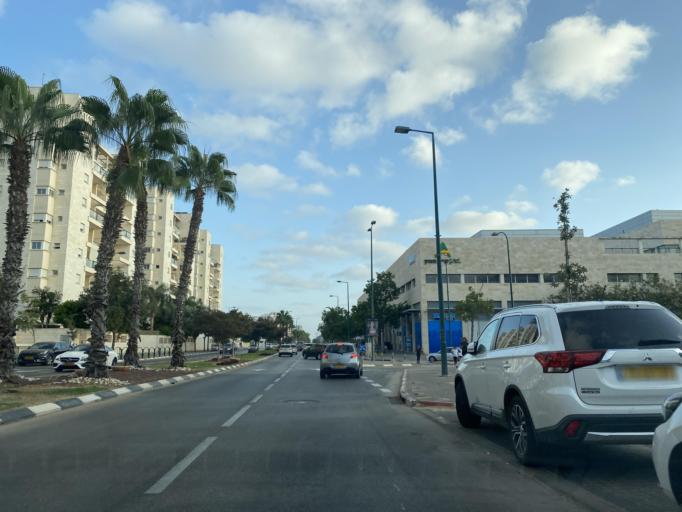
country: IL
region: Central District
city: Netanya
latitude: 32.3081
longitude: 34.8696
